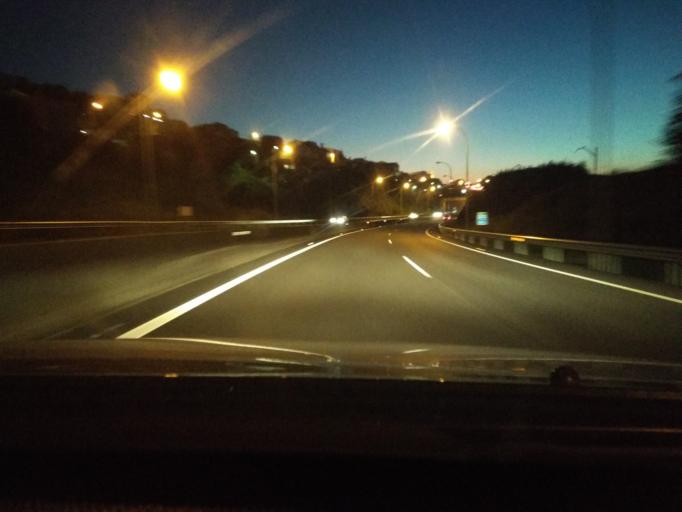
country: ES
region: Galicia
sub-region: Provincia de Pontevedra
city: Vigo
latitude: 42.2504
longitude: -8.6871
